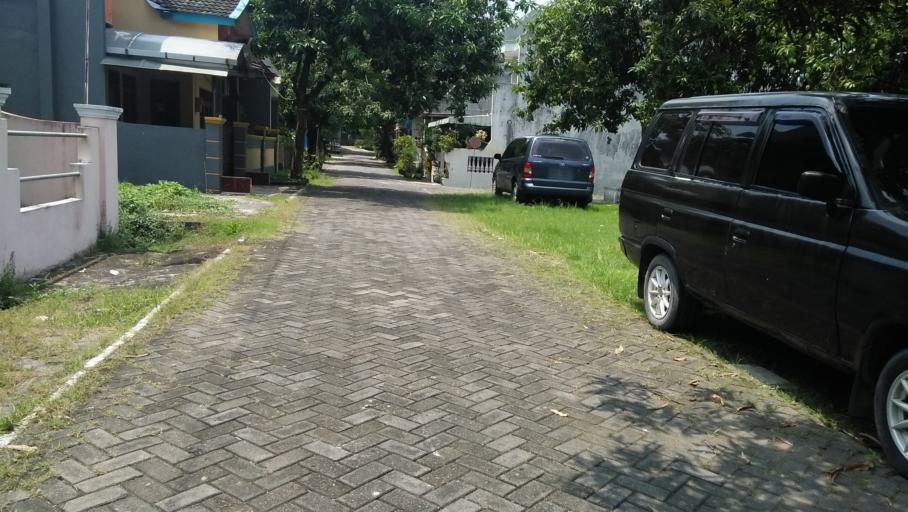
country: ID
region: Central Java
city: Mranggen
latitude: -7.0306
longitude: 110.4623
